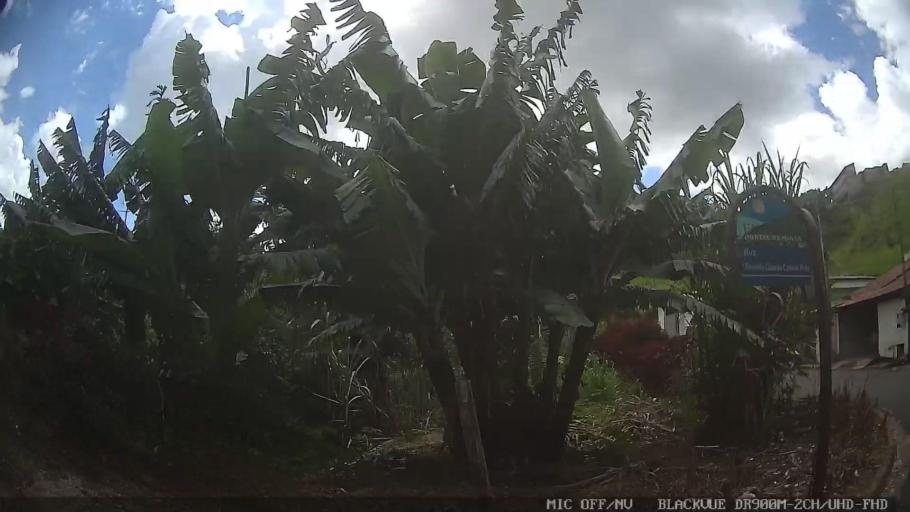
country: BR
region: Minas Gerais
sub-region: Extrema
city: Extrema
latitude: -22.8657
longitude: -46.3317
